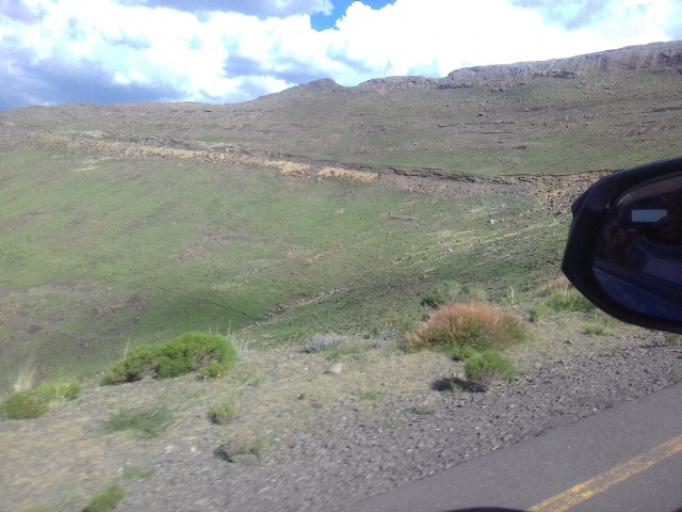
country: LS
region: Thaba-Tseka
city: Thaba-Tseka
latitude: -29.5241
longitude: 28.3433
